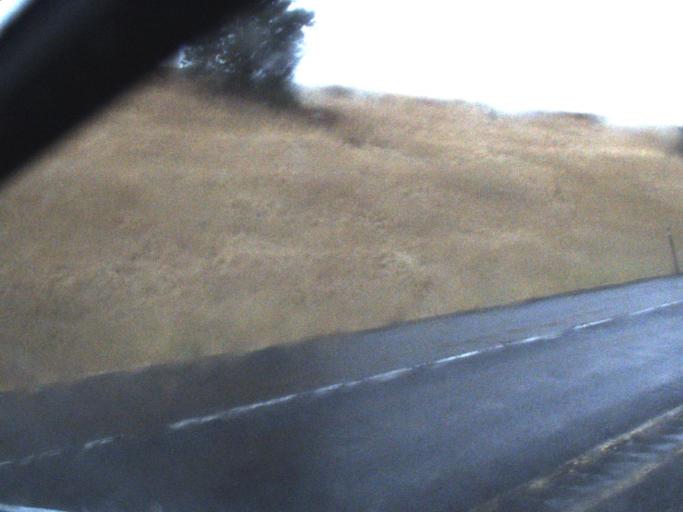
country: US
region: Washington
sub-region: Spokane County
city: Cheney
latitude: 47.2370
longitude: -117.3614
